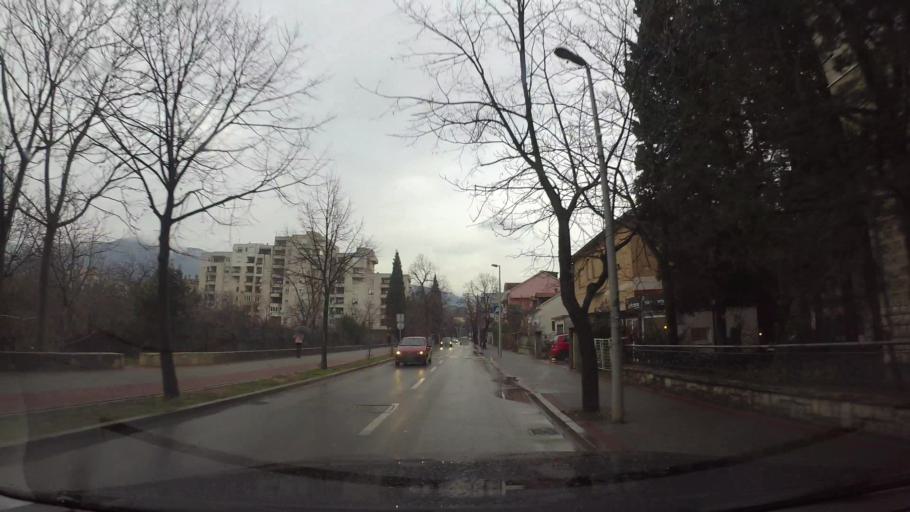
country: BA
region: Federation of Bosnia and Herzegovina
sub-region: Hercegovacko-Bosanski Kanton
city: Mostar
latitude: 43.3430
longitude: 17.8035
